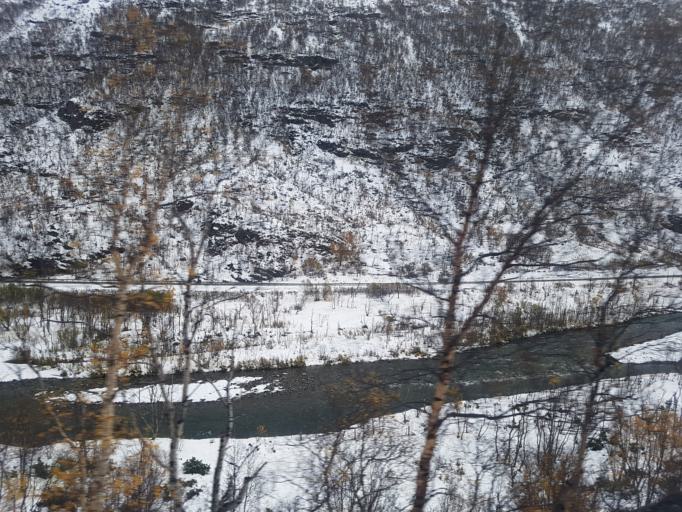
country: NO
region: Sor-Trondelag
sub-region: Oppdal
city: Oppdal
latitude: 62.3348
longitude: 9.6224
